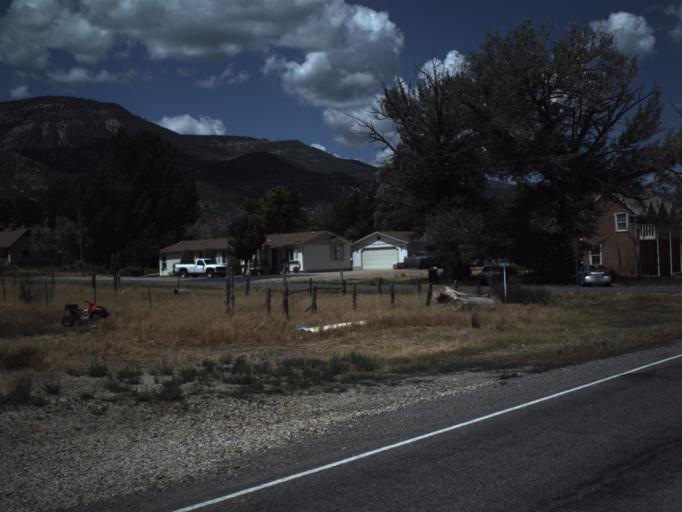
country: US
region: Utah
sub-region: Sanpete County
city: Moroni
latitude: 39.4850
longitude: -111.6351
